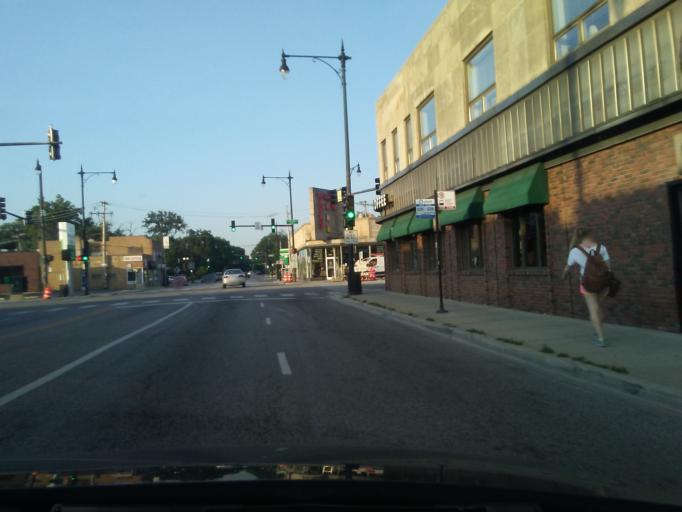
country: US
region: Illinois
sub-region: Cook County
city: Lincolnwood
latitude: 41.9977
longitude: -87.7638
